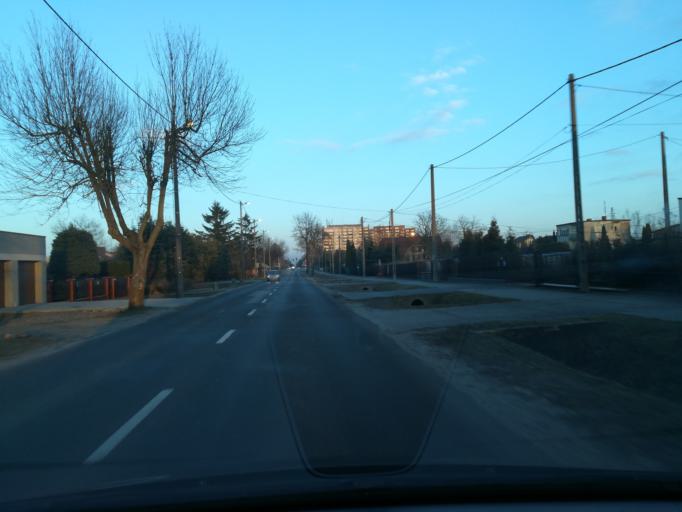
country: PL
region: Lodz Voivodeship
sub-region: Piotrkow Trybunalski
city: Piotrkow Trybunalski
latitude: 51.4109
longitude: 19.6516
